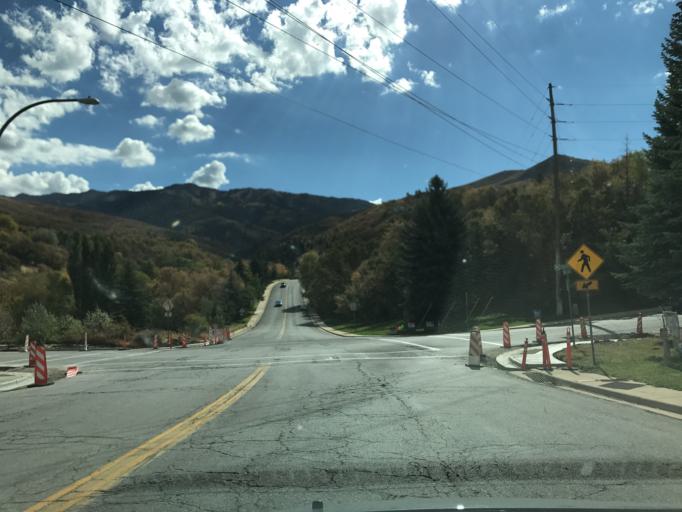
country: US
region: Utah
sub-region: Davis County
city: Bountiful
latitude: 40.8689
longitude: -111.8471
